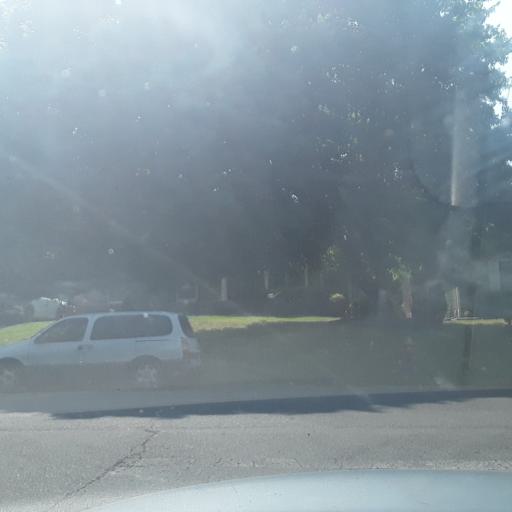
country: US
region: Tennessee
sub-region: Williamson County
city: Brentwood Estates
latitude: 36.0394
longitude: -86.7089
